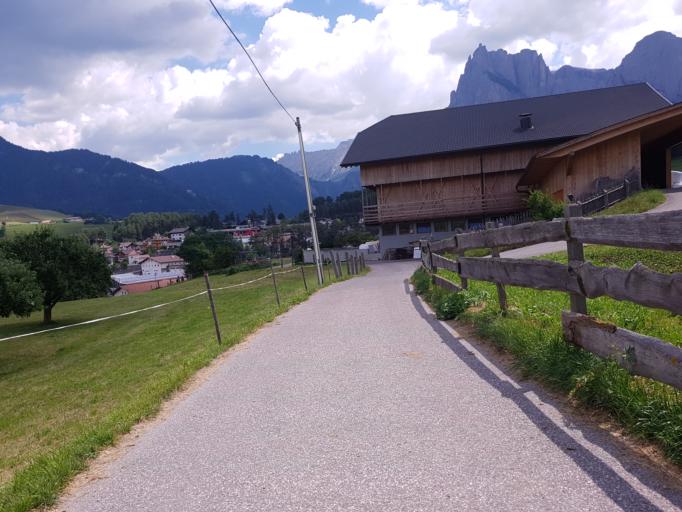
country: IT
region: Trentino-Alto Adige
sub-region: Bolzano
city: Castelrotto
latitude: 46.5587
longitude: 11.5491
